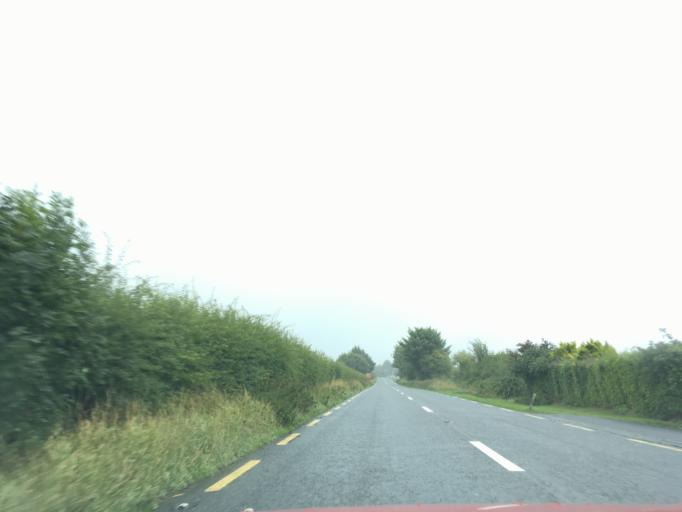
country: IE
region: Munster
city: Carrick-on-Suir
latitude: 52.3512
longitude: -7.4527
